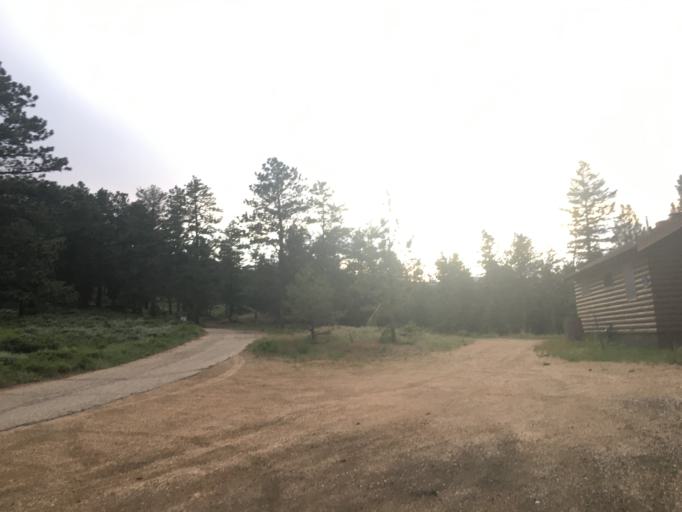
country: US
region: Colorado
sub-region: Larimer County
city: Estes Park
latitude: 40.3379
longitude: -105.5827
